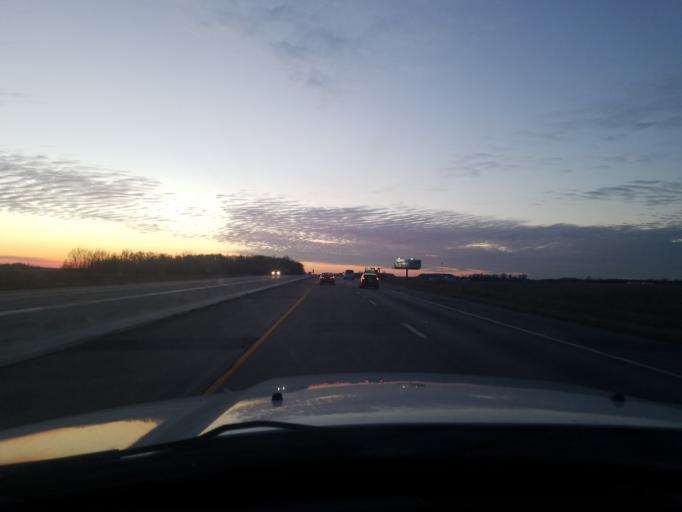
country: US
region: Indiana
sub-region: Wells County
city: Ossian
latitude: 40.9527
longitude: -85.2270
